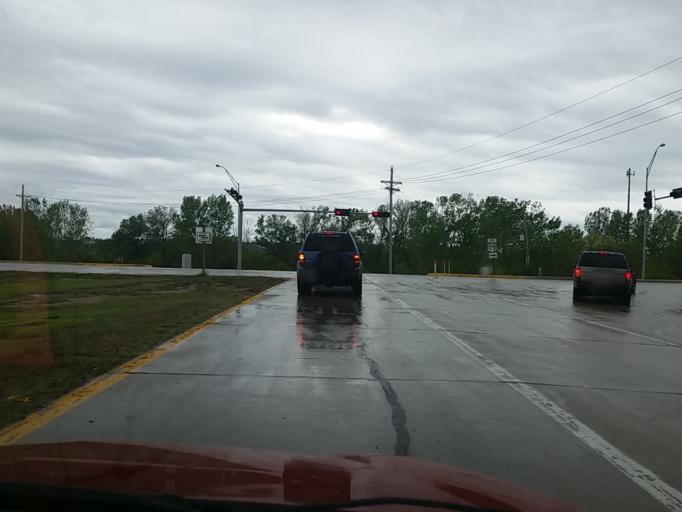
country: US
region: Nebraska
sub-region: Sarpy County
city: Offutt Air Force Base
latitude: 41.1158
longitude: -95.9278
